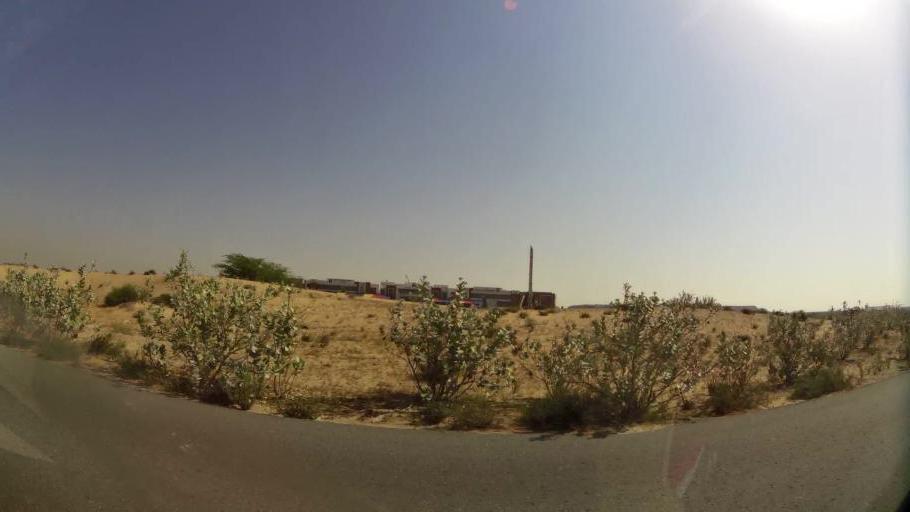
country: AE
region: Ajman
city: Ajman
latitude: 25.4210
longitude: 55.5490
